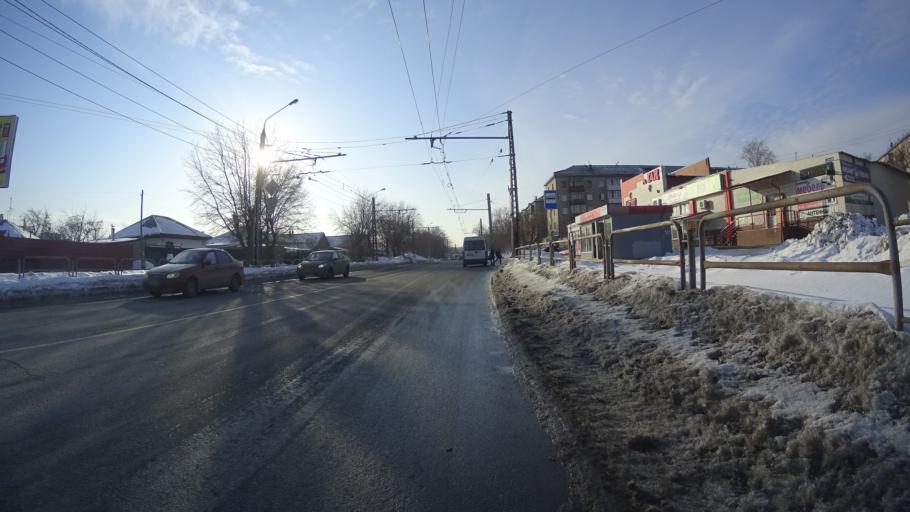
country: RU
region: Chelyabinsk
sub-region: Gorod Chelyabinsk
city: Chelyabinsk
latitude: 55.1838
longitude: 61.4580
